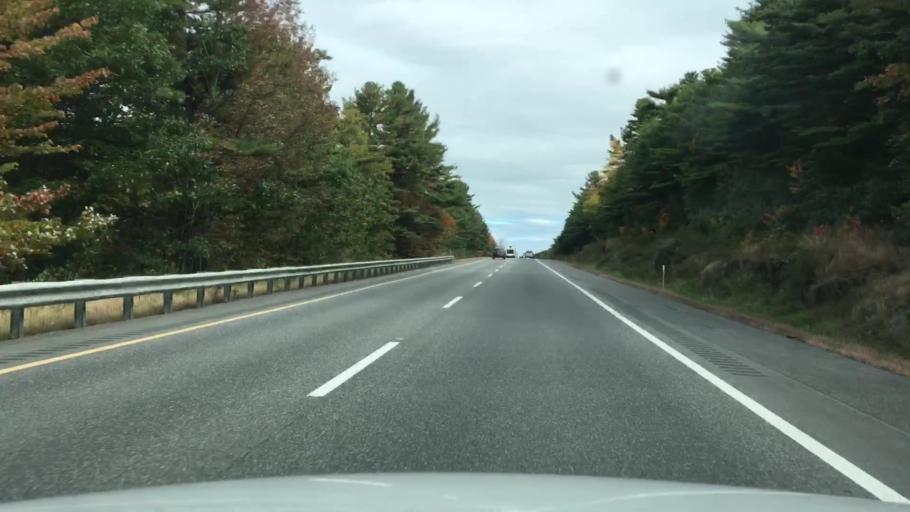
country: US
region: Maine
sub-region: Kennebec County
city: Sidney
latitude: 44.3865
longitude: -69.7620
